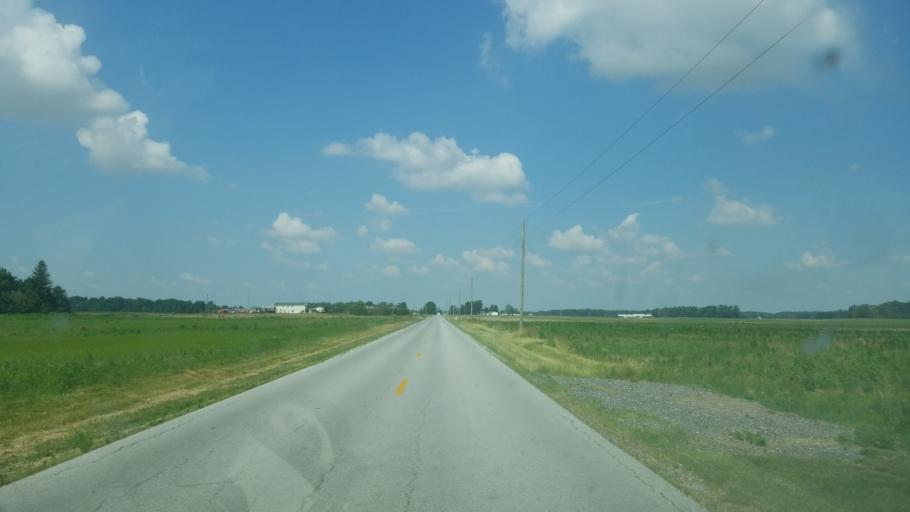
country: US
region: Ohio
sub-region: Auglaize County
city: Wapakoneta
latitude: 40.5703
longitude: -84.1385
